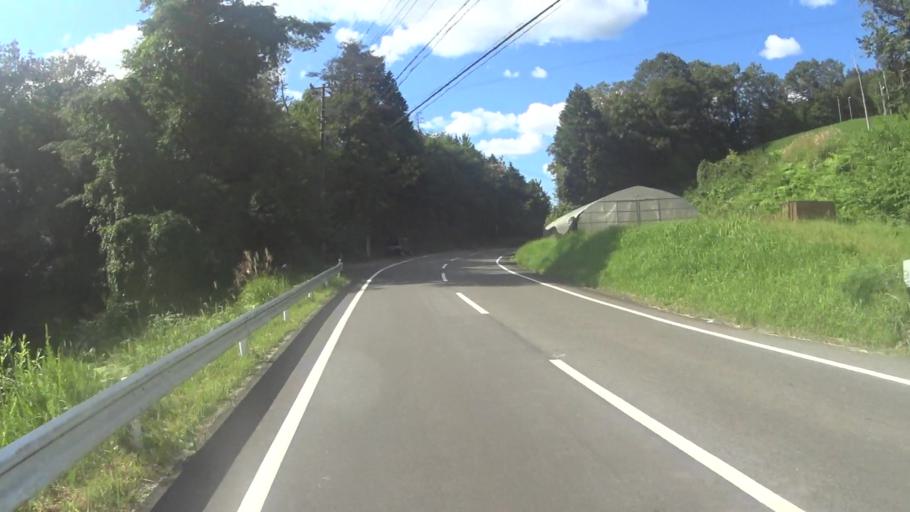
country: JP
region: Mie
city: Ueno-ebisumachi
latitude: 34.7265
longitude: 136.0232
